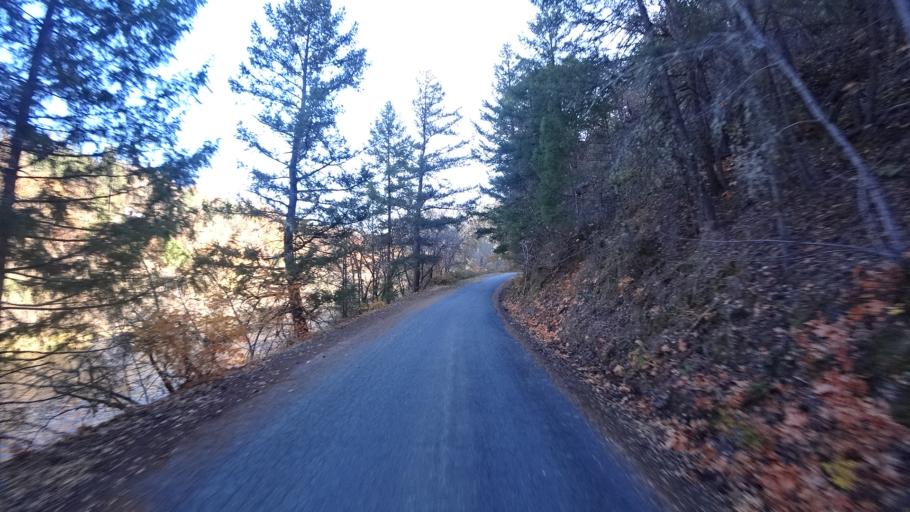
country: US
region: California
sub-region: Siskiyou County
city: Yreka
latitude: 41.8407
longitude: -122.9209
